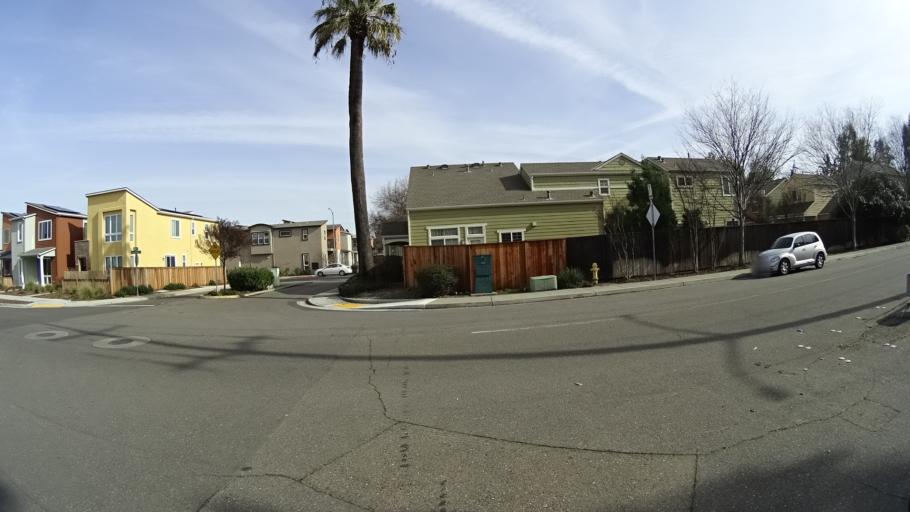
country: US
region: California
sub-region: Yolo County
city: Davis
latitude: 38.5461
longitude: -121.7134
